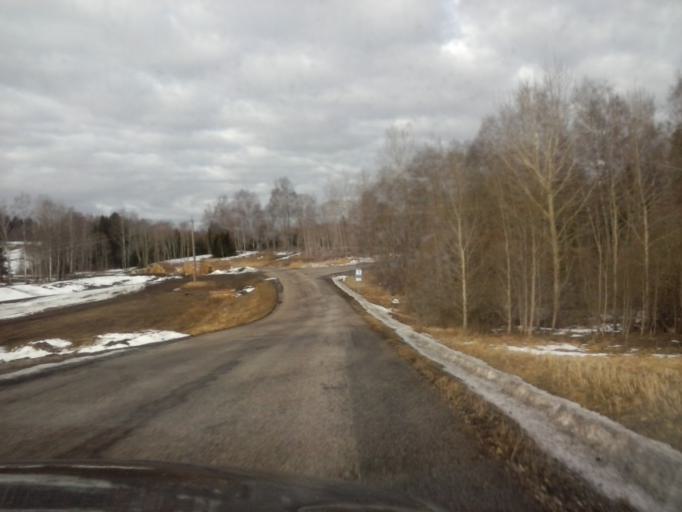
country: EE
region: Tartu
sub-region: Elva linn
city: Elva
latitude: 58.0215
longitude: 26.3302
